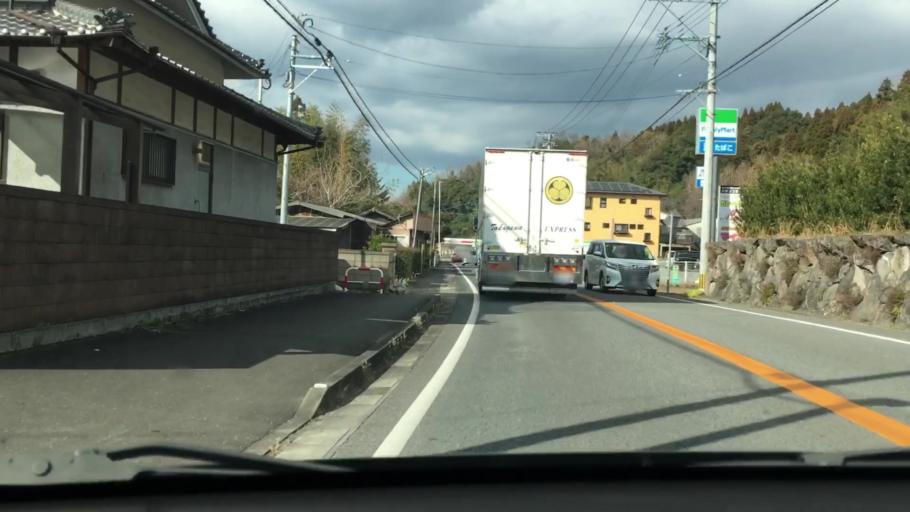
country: JP
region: Oita
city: Usuki
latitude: 33.0469
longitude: 131.6916
